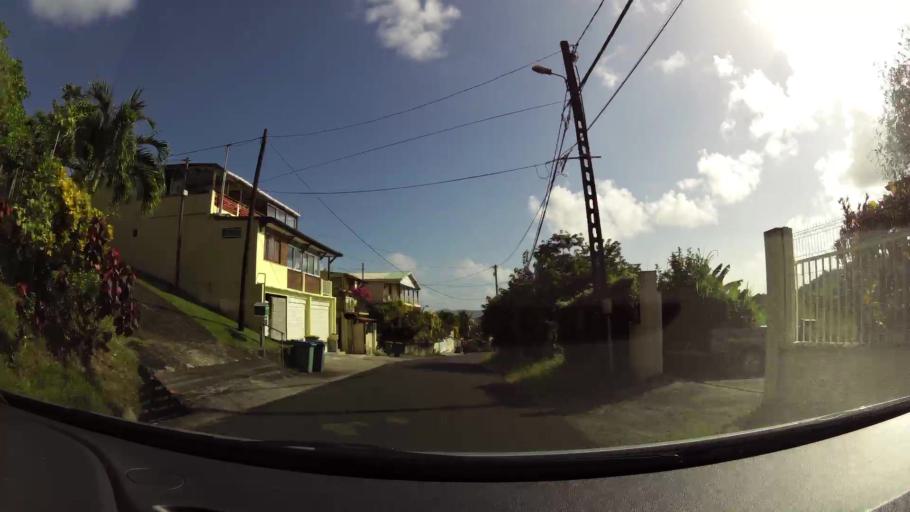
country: MQ
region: Martinique
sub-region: Martinique
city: La Trinite
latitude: 14.7370
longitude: -60.9706
